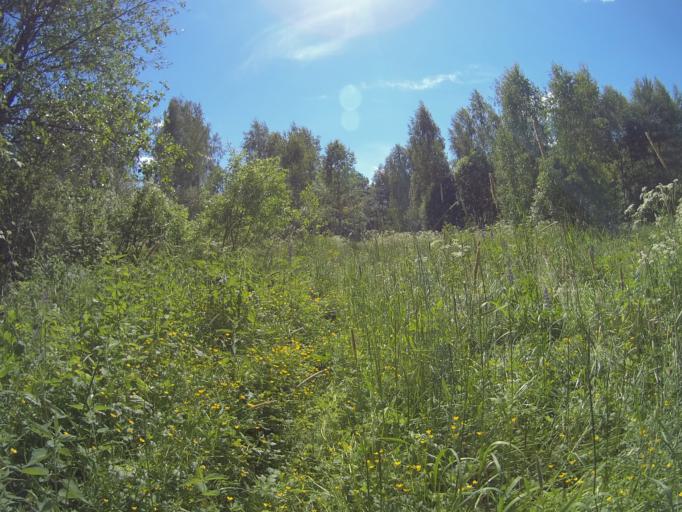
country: RU
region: Vladimir
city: Golovino
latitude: 55.9983
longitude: 40.4178
